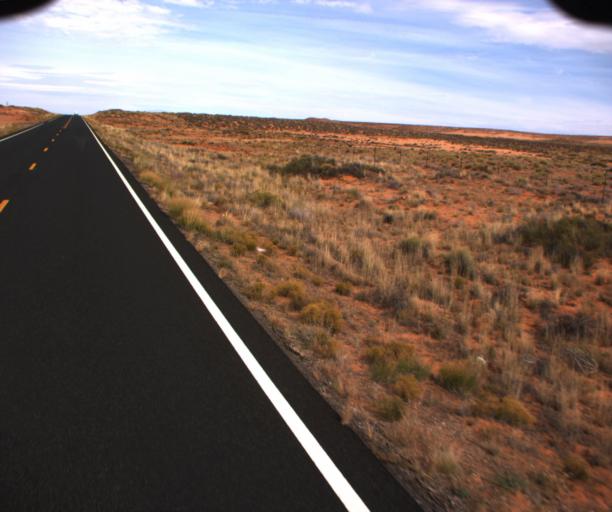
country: US
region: Arizona
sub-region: Apache County
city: Many Farms
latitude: 36.8532
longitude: -109.6377
